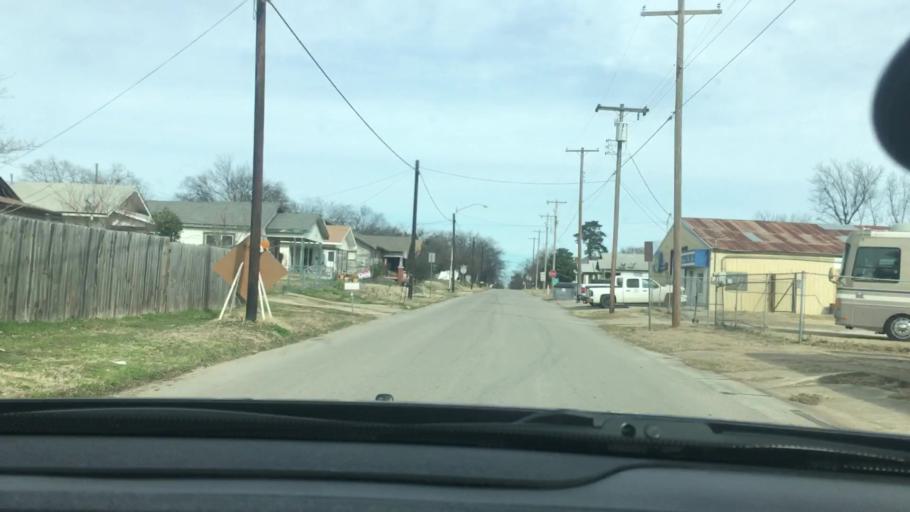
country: US
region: Oklahoma
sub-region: Carter County
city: Ardmore
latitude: 34.1767
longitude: -97.1249
